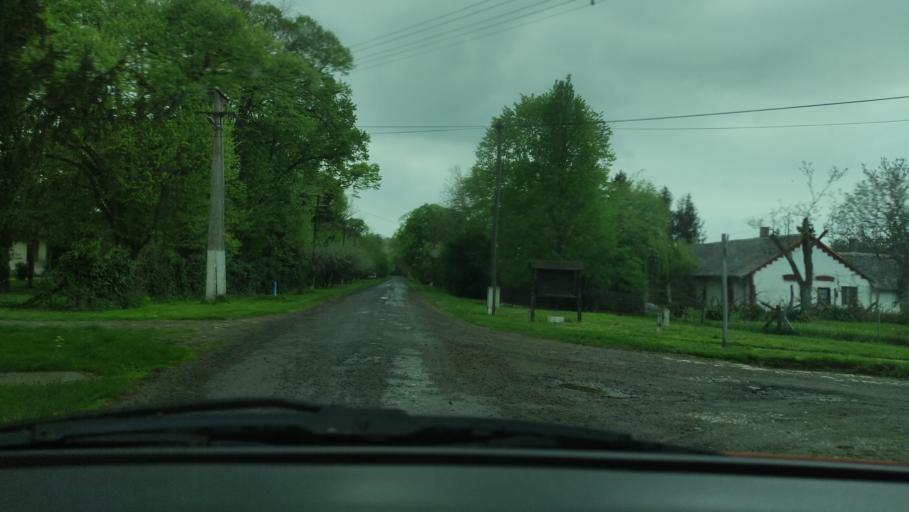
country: HR
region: Osjecko-Baranjska
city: Batina
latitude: 45.9070
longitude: 18.7620
